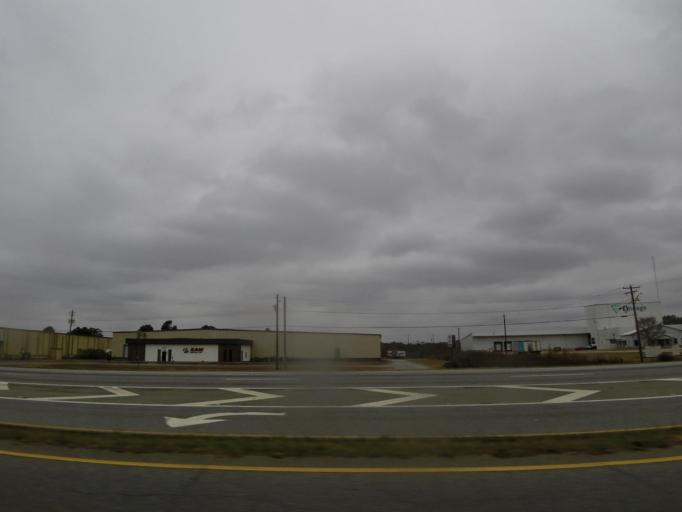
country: US
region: Georgia
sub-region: Dougherty County
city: Albany
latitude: 31.5568
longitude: -84.1151
